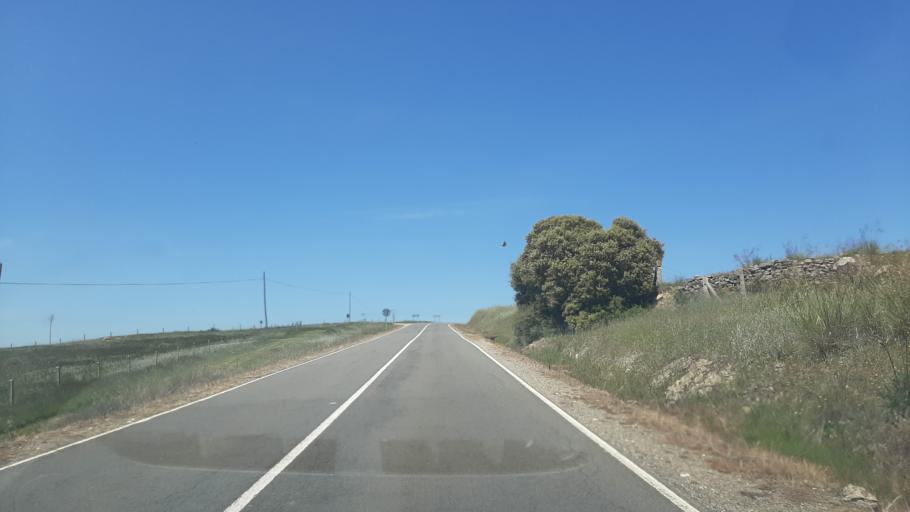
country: ES
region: Castille and Leon
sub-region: Provincia de Salamanca
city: Salvatierra de Tormes
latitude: 40.5368
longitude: -5.5717
